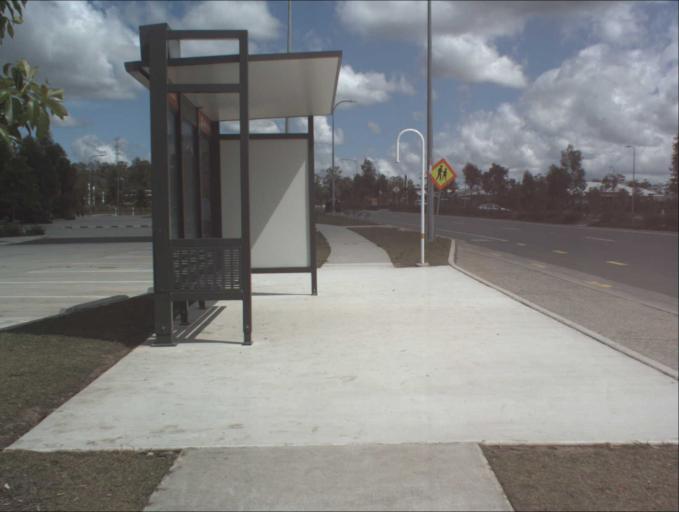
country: AU
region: Queensland
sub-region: Logan
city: Chambers Flat
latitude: -27.8022
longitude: 153.1058
